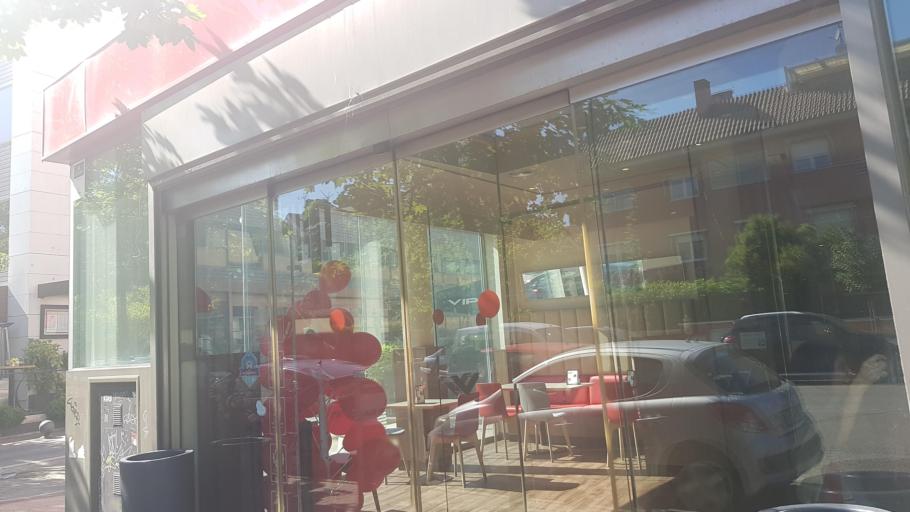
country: ES
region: Madrid
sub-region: Provincia de Madrid
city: Pozuelo de Alarcon
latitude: 40.4650
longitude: -3.7859
